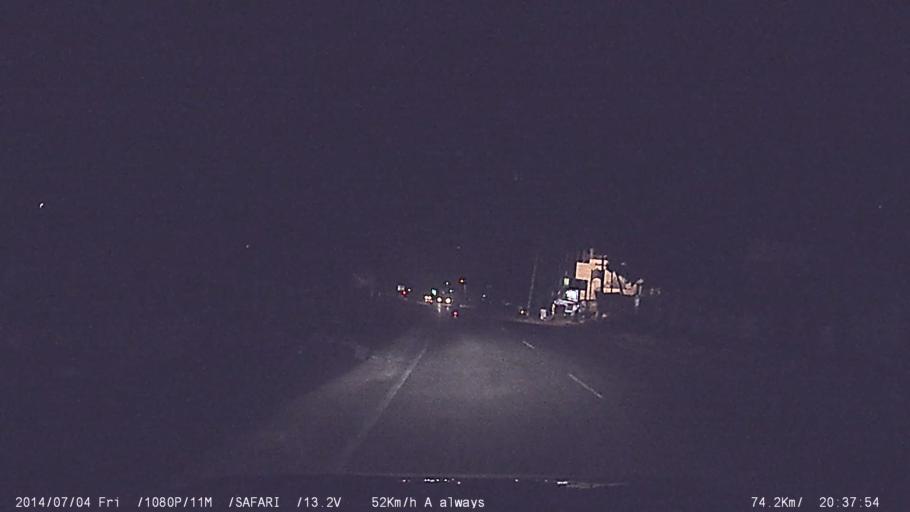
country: IN
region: Tamil Nadu
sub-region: Coimbatore
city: Madukkarai
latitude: 10.9030
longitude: 76.9422
